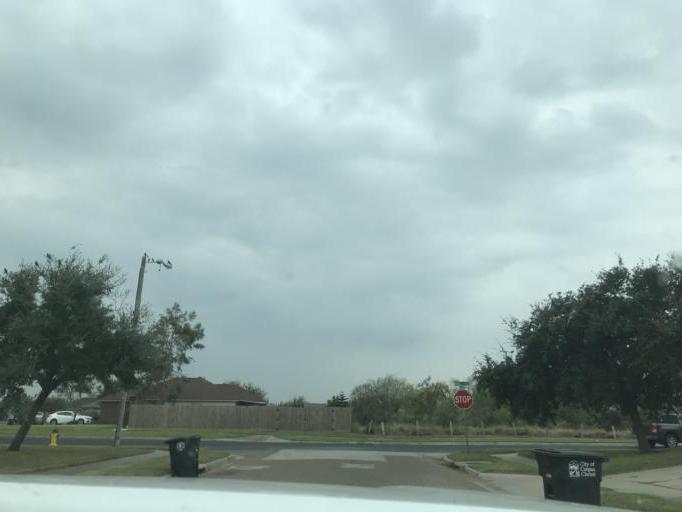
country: US
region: Texas
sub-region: Nueces County
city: Corpus Christi
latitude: 27.6665
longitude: -97.3418
